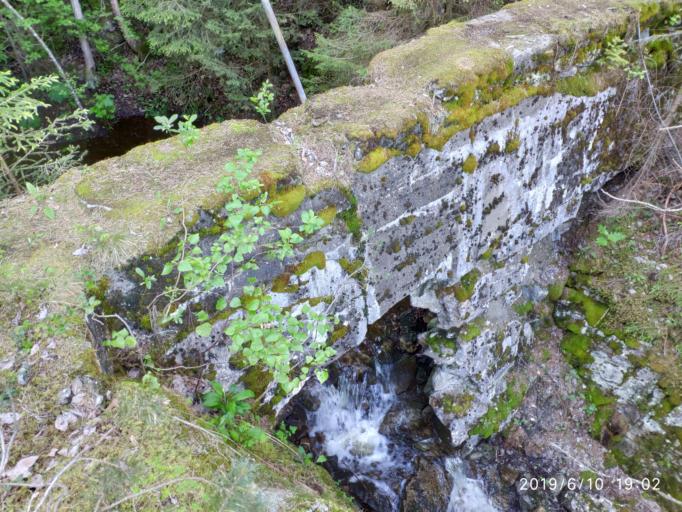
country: NO
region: Oppland
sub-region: Jevnaker
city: Jevnaker
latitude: 60.2502
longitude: 10.3652
